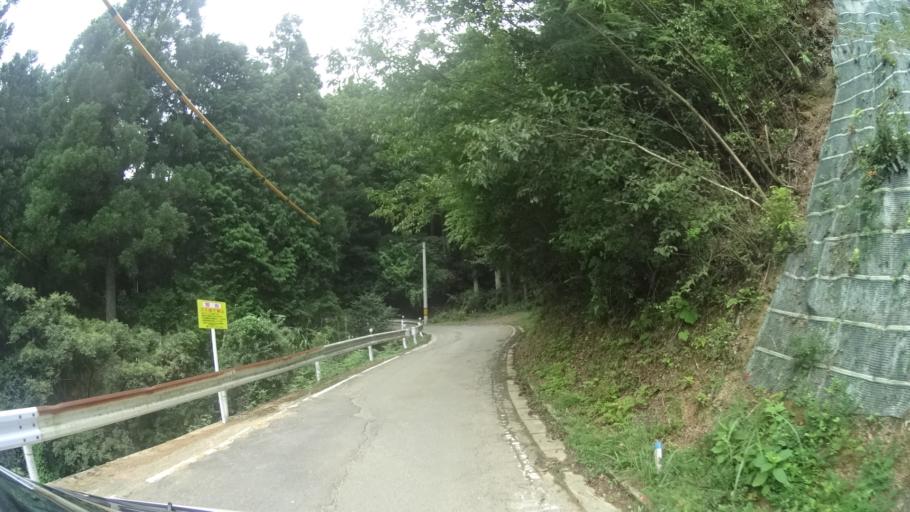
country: JP
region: Kyoto
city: Maizuru
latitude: 35.3539
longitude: 135.3415
